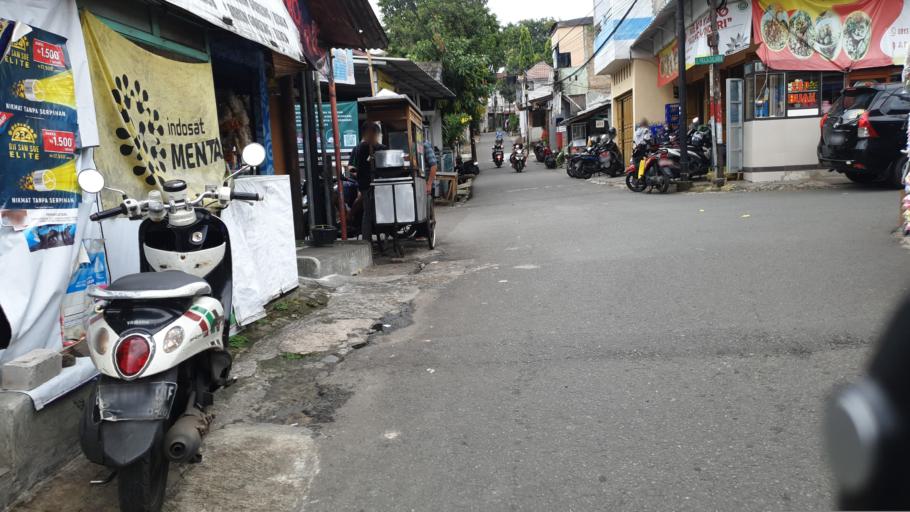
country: ID
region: Jakarta Raya
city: Jakarta
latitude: -6.2530
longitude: 106.7831
